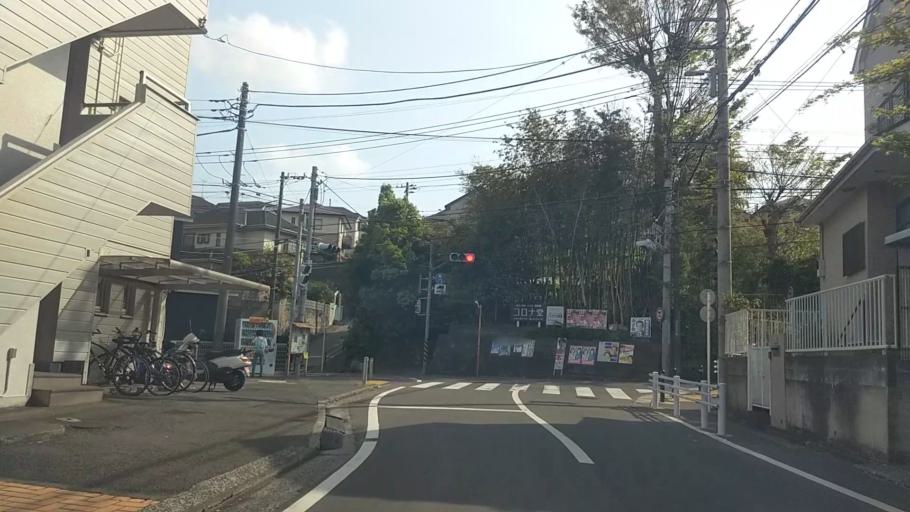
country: JP
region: Kanagawa
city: Kamakura
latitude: 35.3726
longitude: 139.5535
